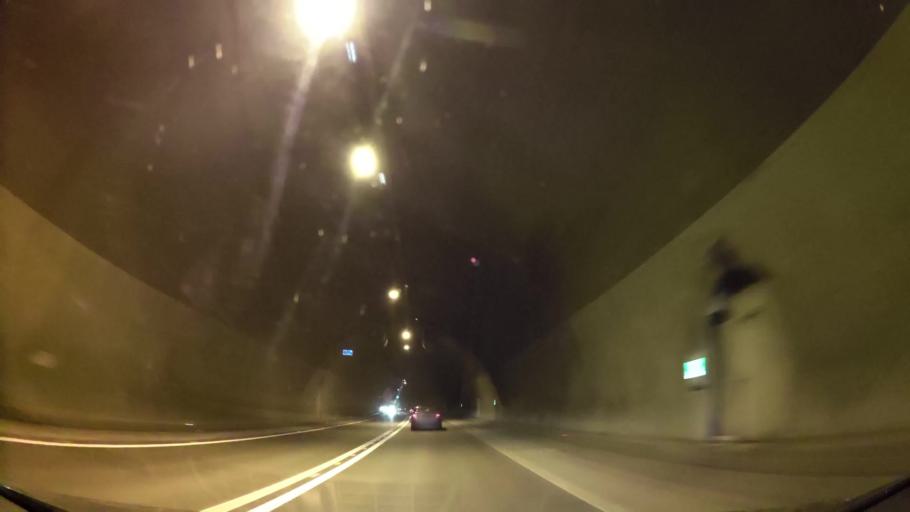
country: RS
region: Central Serbia
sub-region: Belgrade
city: Rakovica
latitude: 44.7210
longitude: 20.4556
